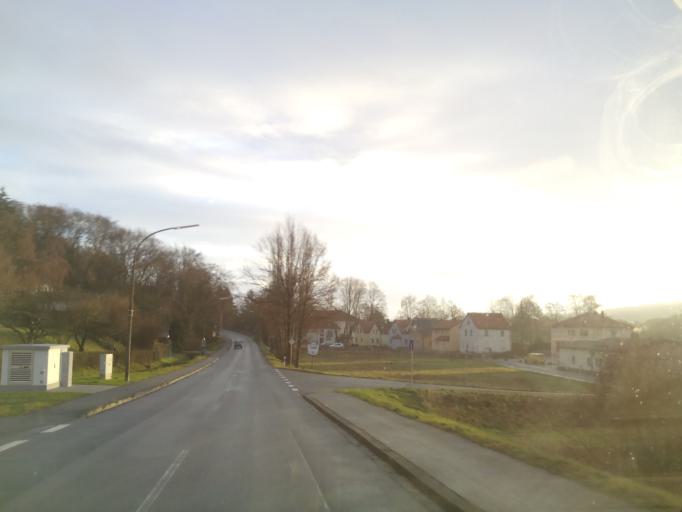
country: DE
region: Bavaria
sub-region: Upper Franconia
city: Lichtenfels
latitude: 50.1562
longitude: 11.0627
